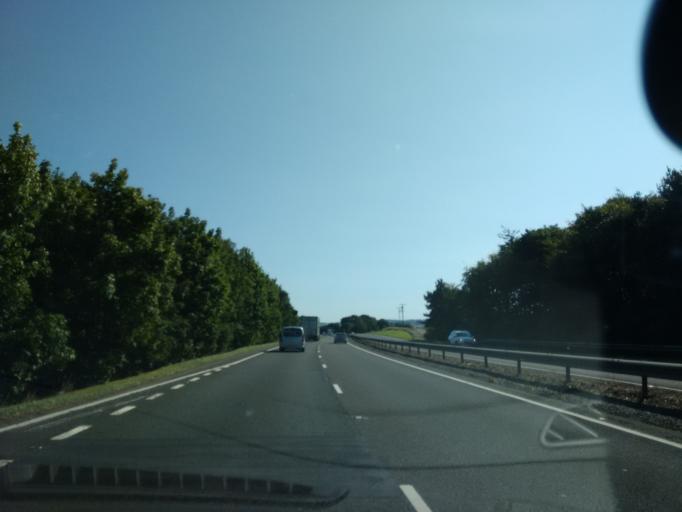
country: GB
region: England
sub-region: Northumberland
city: Corbridge
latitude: 54.9787
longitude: -1.9877
